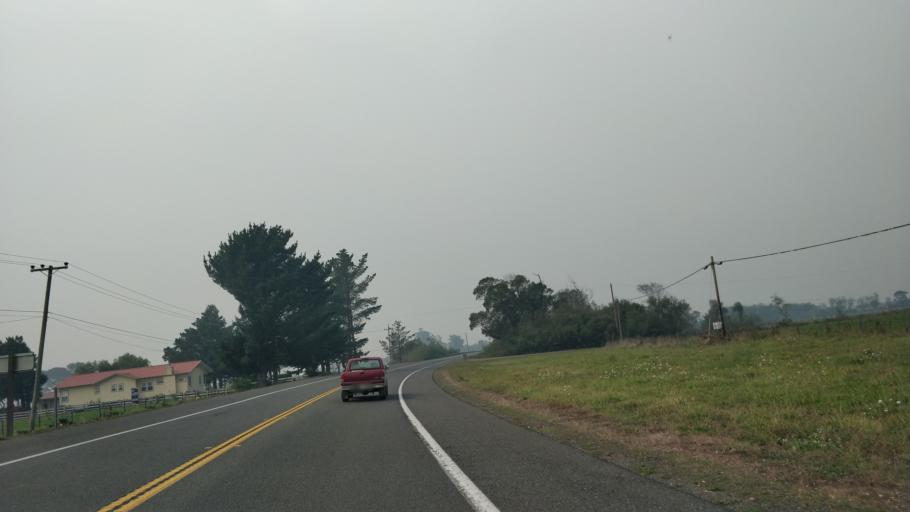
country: US
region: California
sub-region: Humboldt County
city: Ferndale
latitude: 40.5954
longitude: -124.2381
